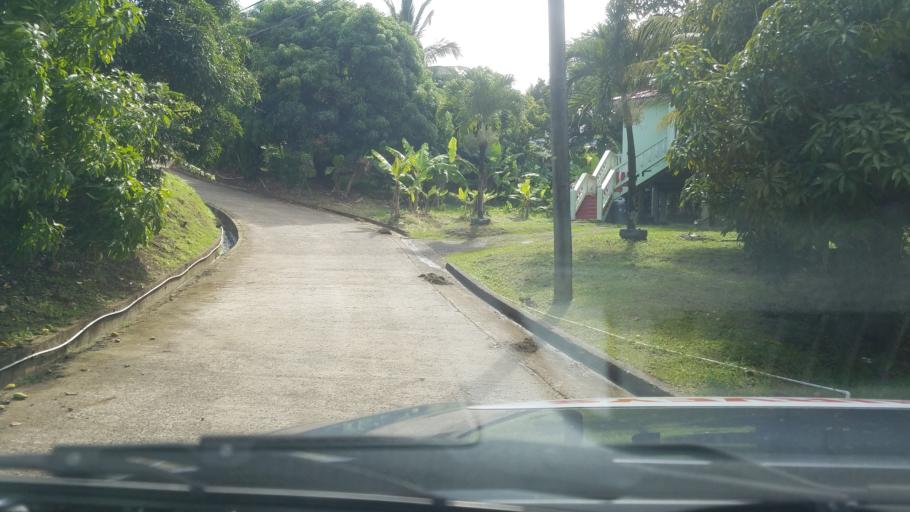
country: LC
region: Castries Quarter
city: Bisee
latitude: 14.0191
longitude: -60.9739
